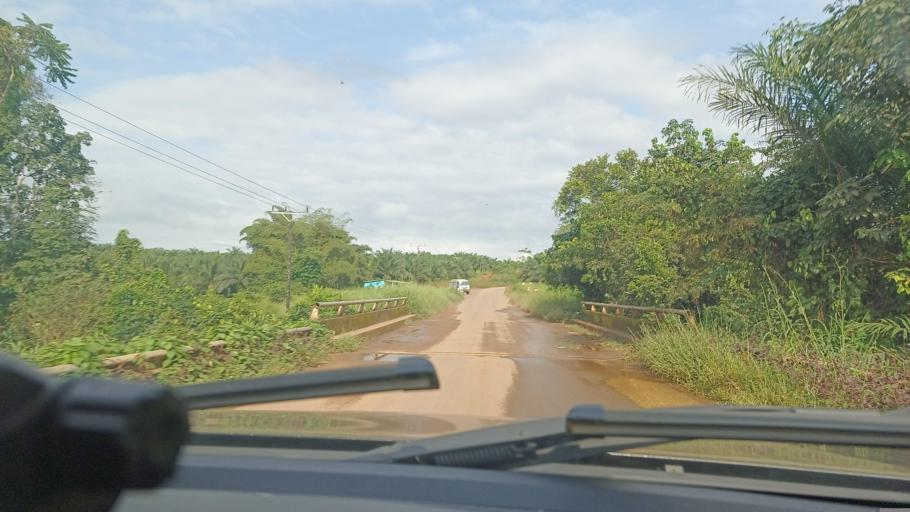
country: LR
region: Bomi
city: Tubmanburg
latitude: 6.7025
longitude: -10.9199
